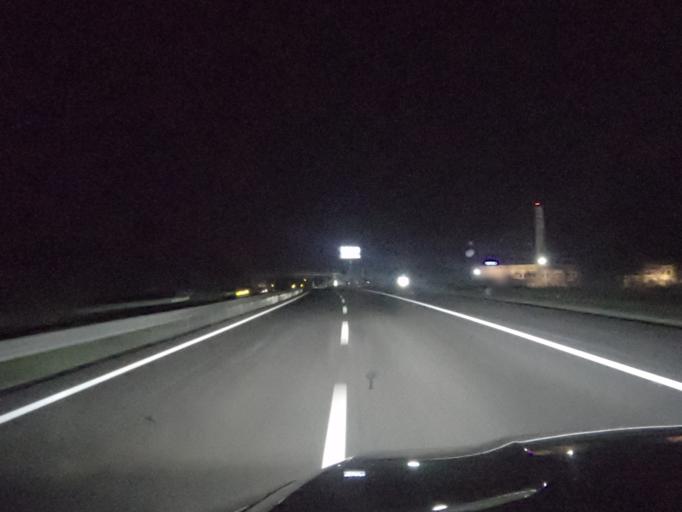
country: PT
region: Aveiro
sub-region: Mealhada
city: Mealhada
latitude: 40.3623
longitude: -8.4925
